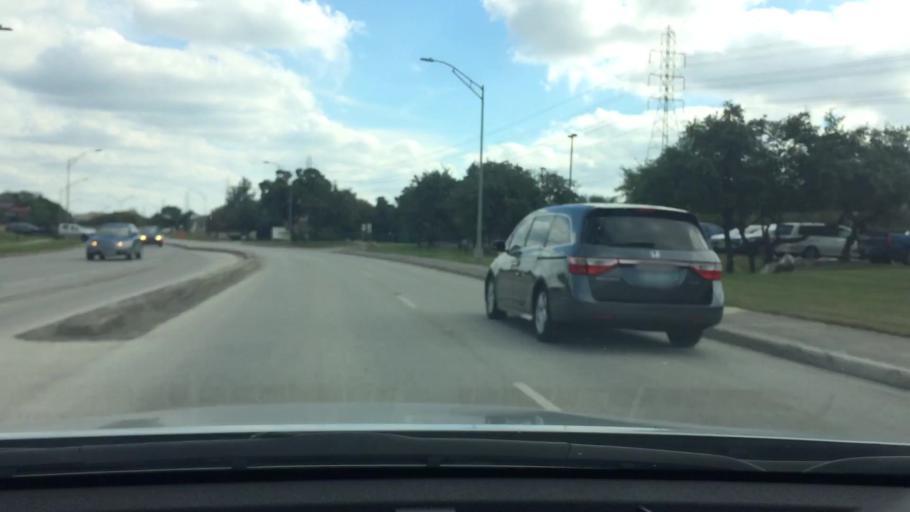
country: US
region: Texas
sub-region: Bexar County
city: Shavano Park
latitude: 29.5864
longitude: -98.5719
